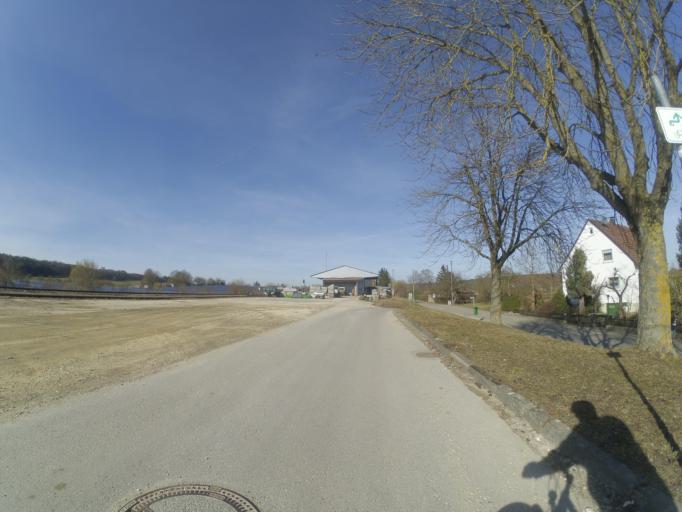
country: DE
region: Baden-Wuerttemberg
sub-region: Regierungsbezirk Stuttgart
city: Sontheim an der Brenz
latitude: 48.5606
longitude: 10.2851
